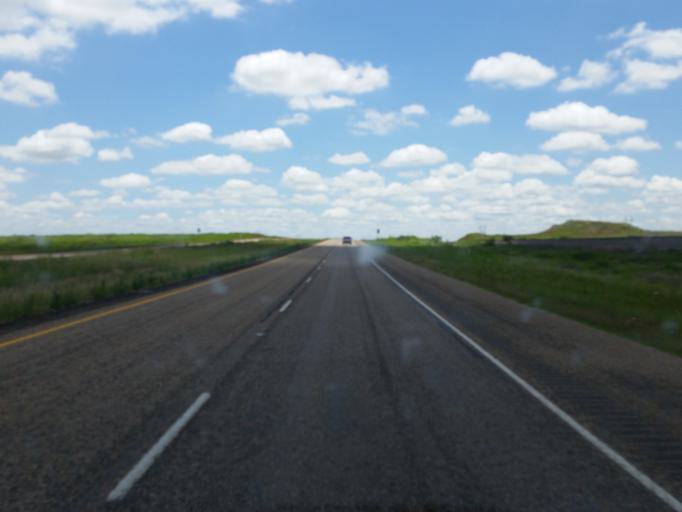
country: US
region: Texas
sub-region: Garza County
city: Post
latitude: 33.1210
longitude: -101.2834
